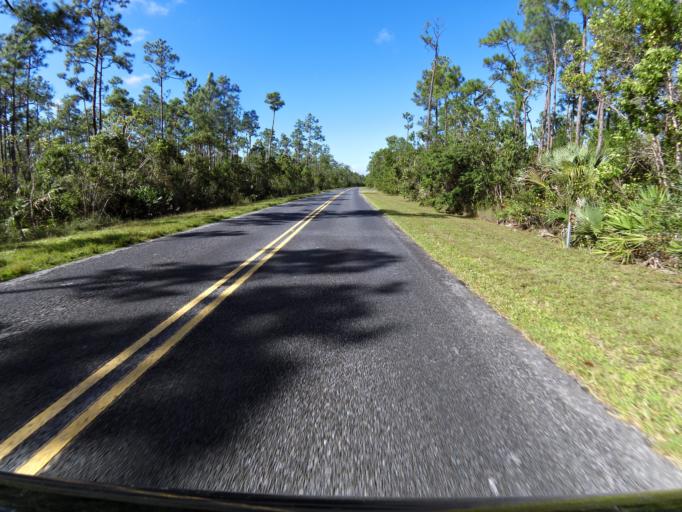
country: US
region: Florida
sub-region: Miami-Dade County
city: Florida City
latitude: 25.4225
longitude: -80.6795
